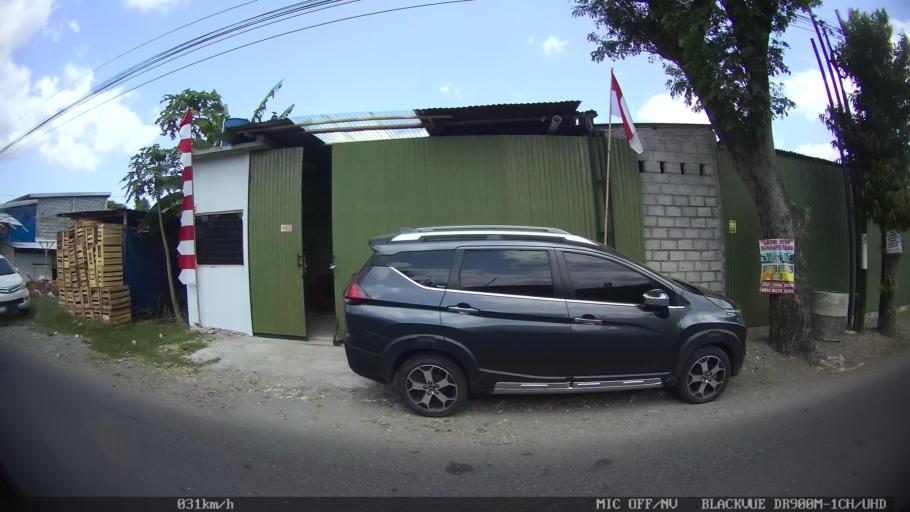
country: ID
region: Daerah Istimewa Yogyakarta
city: Sewon
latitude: -7.8707
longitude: 110.3578
